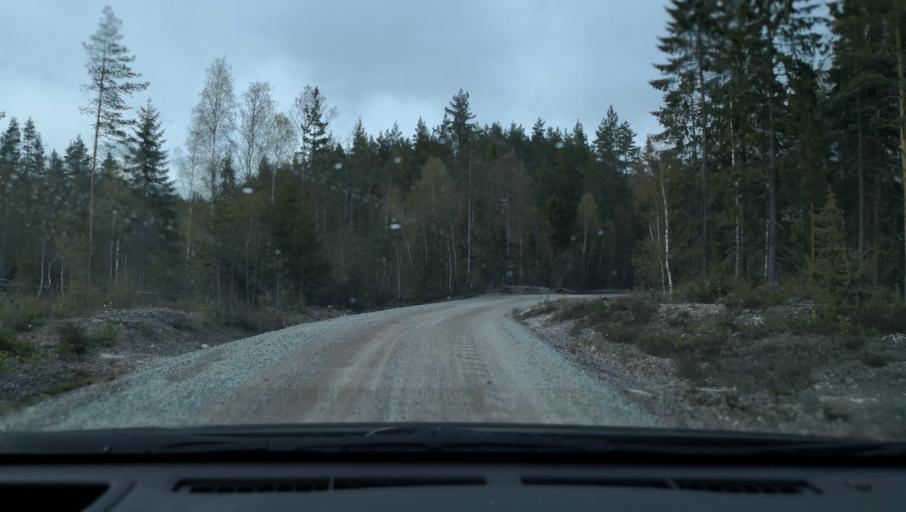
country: SE
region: Dalarna
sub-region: Saters Kommun
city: Saeter
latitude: 60.1870
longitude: 15.7332
